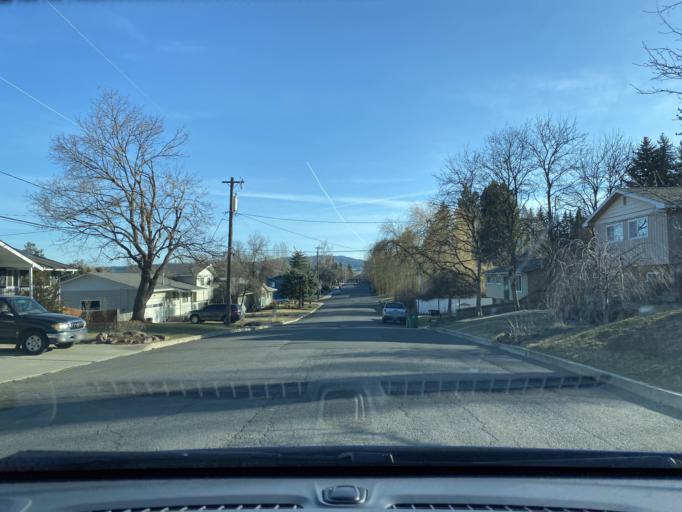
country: US
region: Idaho
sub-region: Latah County
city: Moscow
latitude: 46.7436
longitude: -116.9831
